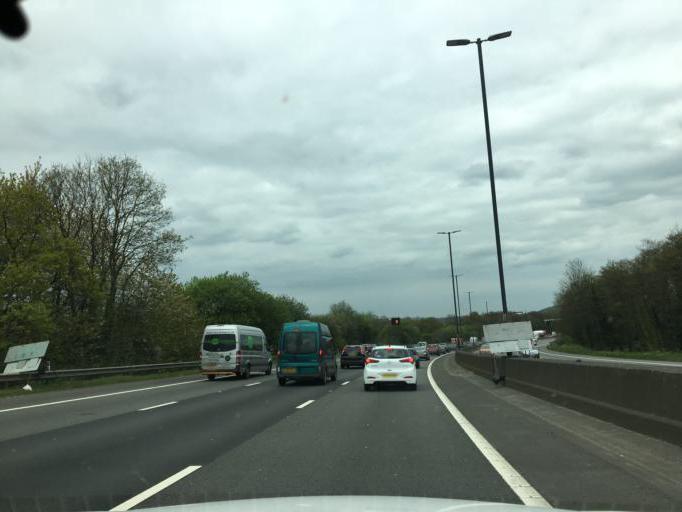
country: GB
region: Wales
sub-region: Newport
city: Newport
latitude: 51.5908
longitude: -3.0306
